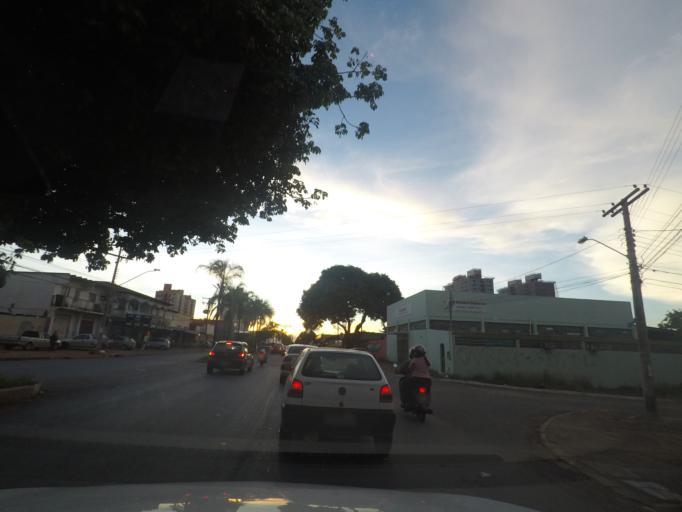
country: BR
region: Goias
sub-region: Goiania
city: Goiania
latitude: -16.6964
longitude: -49.3068
